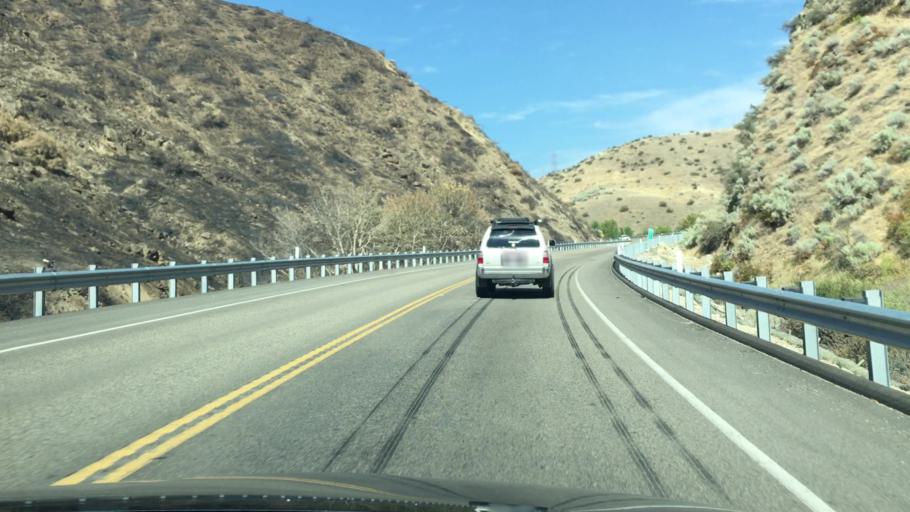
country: US
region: Idaho
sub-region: Ada County
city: Eagle
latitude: 43.7604
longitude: -116.2717
